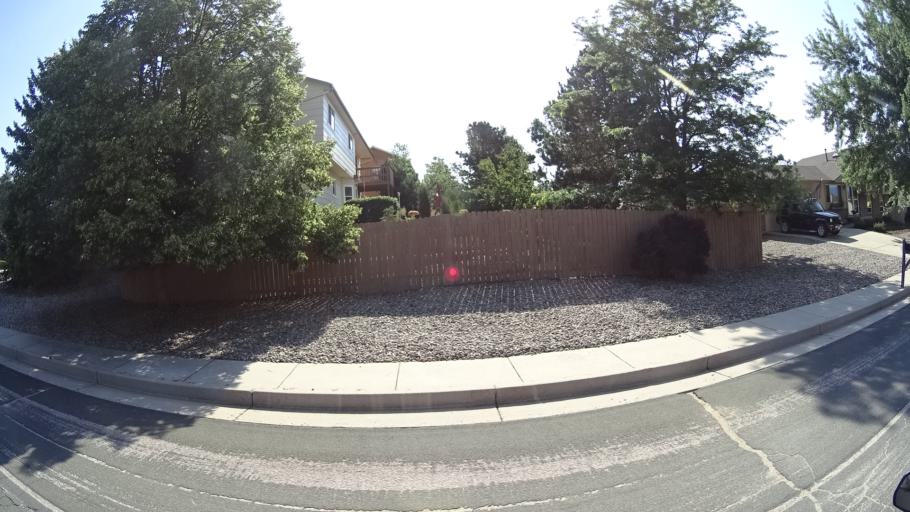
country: US
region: Colorado
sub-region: El Paso County
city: Air Force Academy
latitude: 38.9572
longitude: -104.7837
